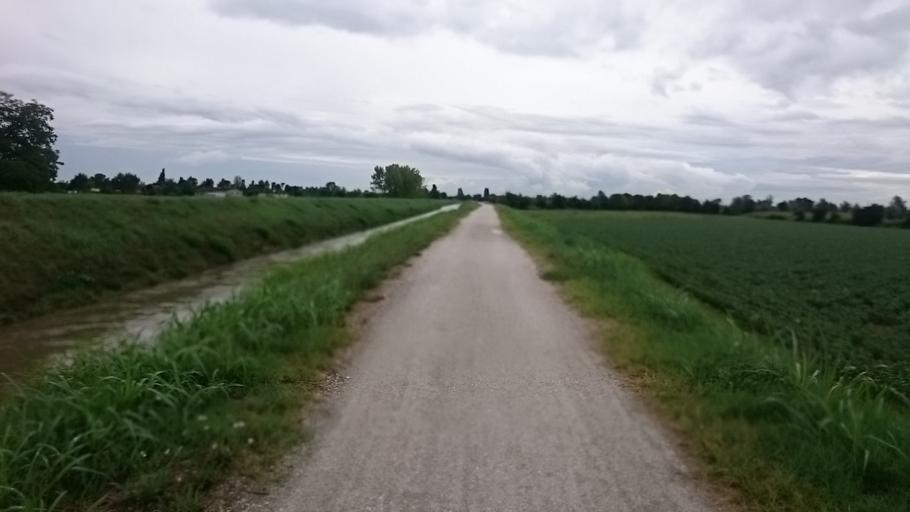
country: IT
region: Veneto
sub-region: Provincia di Padova
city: Loreggiola
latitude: 45.6124
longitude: 11.9293
